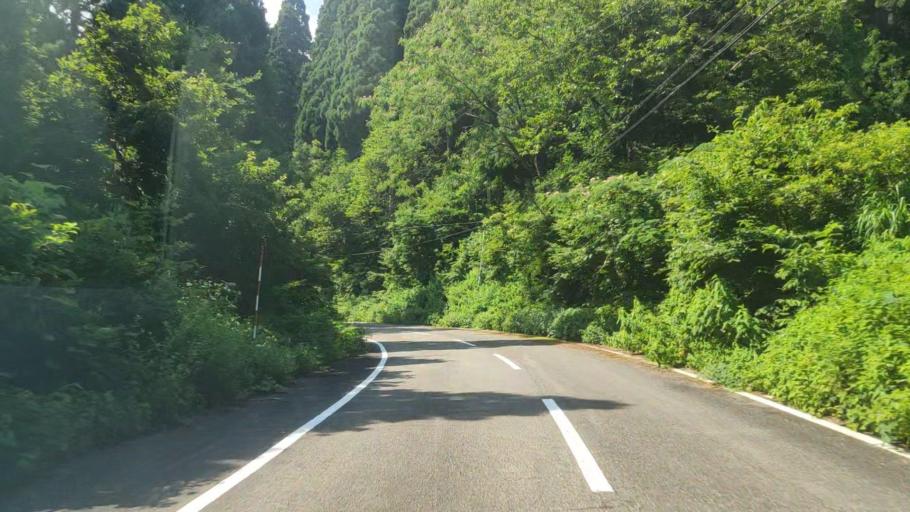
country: JP
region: Fukui
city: Katsuyama
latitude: 36.2312
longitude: 136.5304
